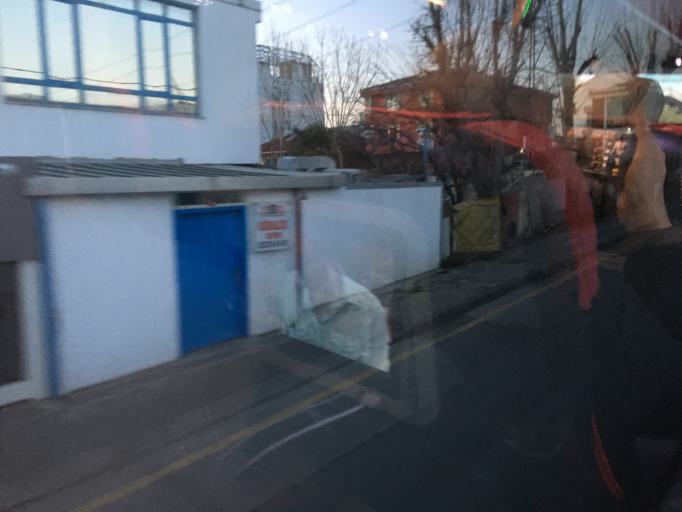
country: TR
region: Istanbul
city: Umraniye
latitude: 40.9976
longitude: 29.1485
